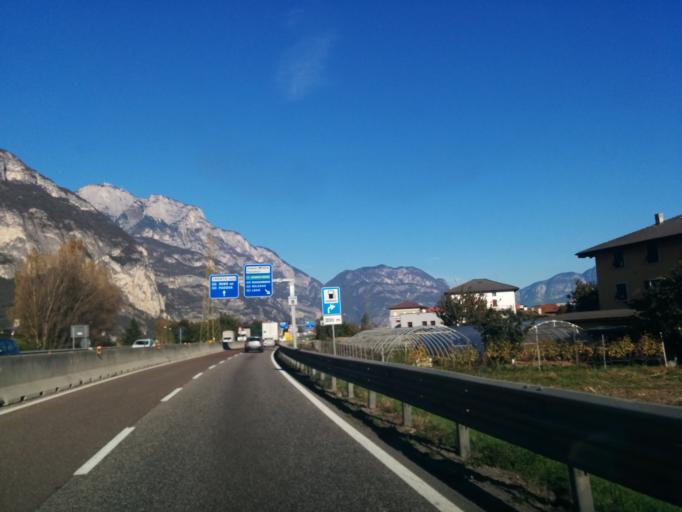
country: IT
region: Trentino-Alto Adige
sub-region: Provincia di Trento
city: Trento
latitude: 46.0883
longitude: 11.1043
